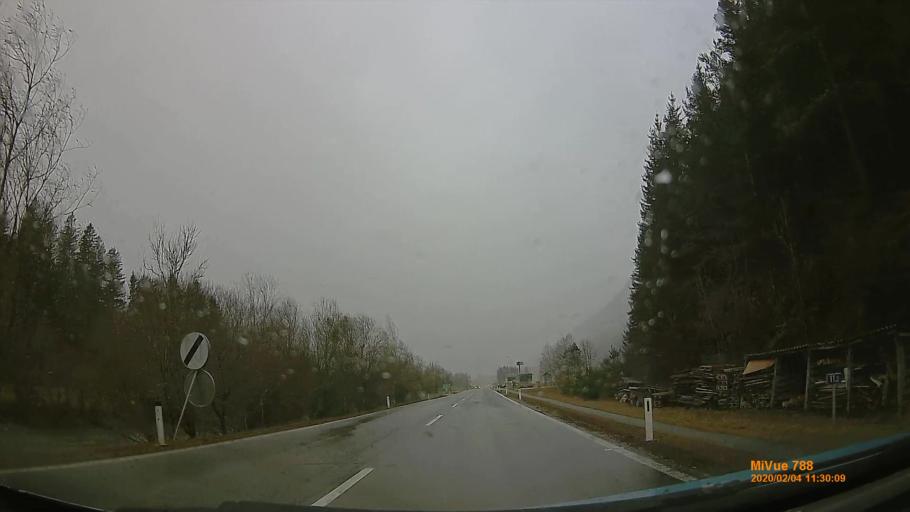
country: AT
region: Styria
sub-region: Politischer Bezirk Bruck-Muerzzuschlag
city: Kapellen
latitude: 47.6544
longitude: 15.6059
